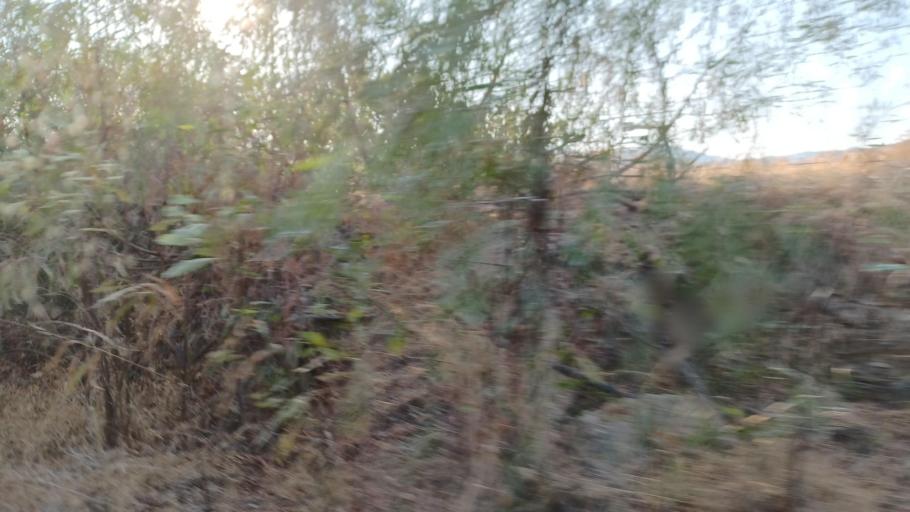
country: CY
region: Pafos
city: Polis
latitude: 35.0480
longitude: 32.4566
